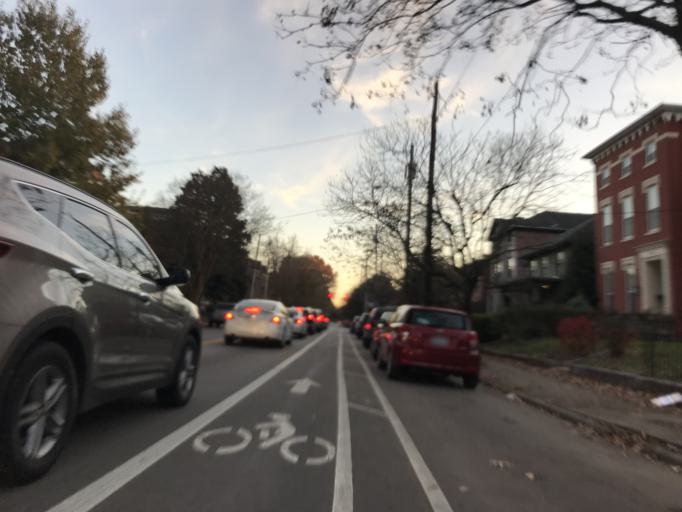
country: US
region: Kentucky
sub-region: Jefferson County
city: Louisville
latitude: 38.2355
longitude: -85.7553
